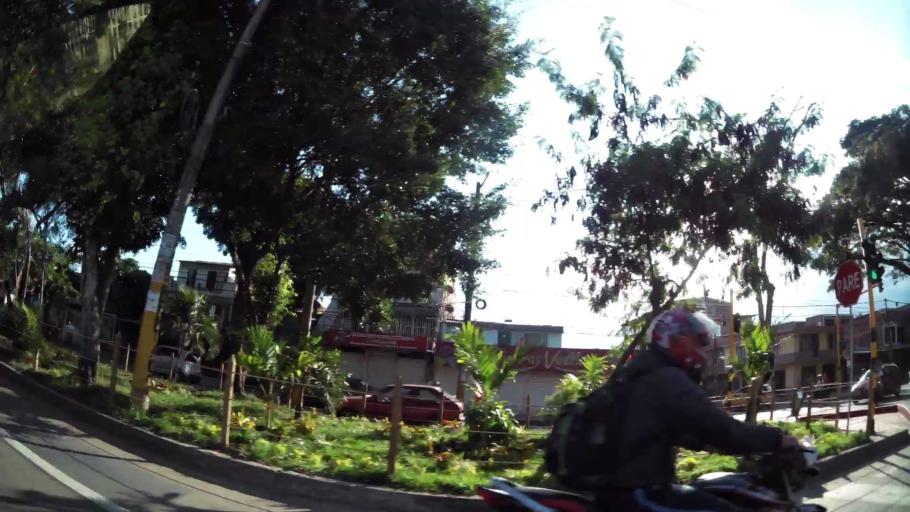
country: CO
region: Valle del Cauca
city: Cali
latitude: 3.4061
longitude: -76.5088
